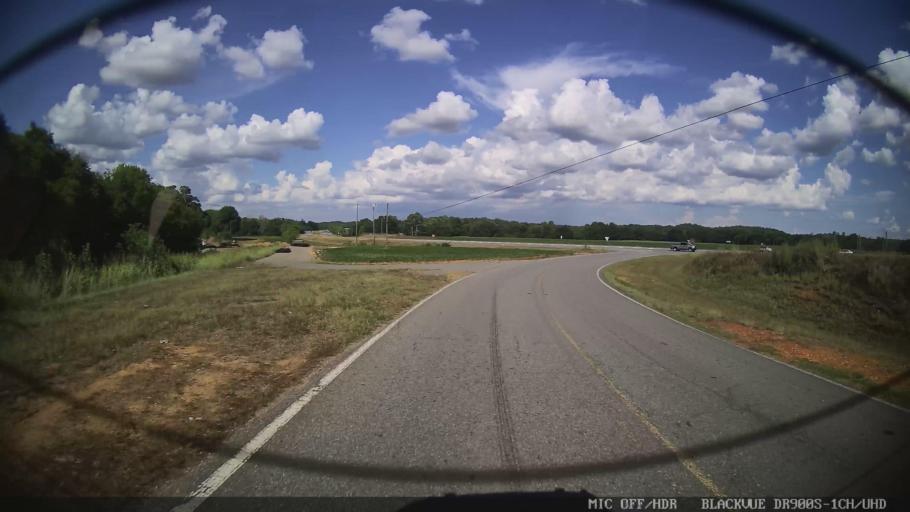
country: US
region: Georgia
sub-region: Bartow County
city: Euharlee
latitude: 34.0929
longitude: -84.9609
